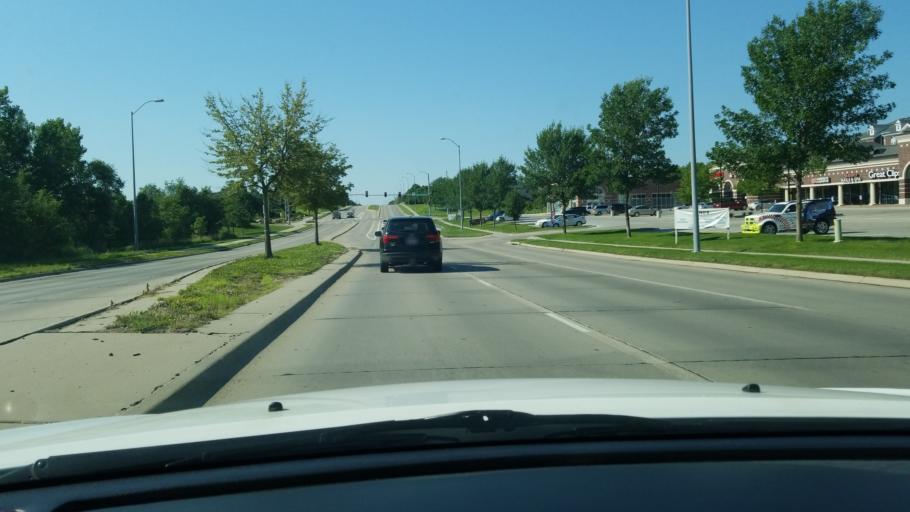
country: US
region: Nebraska
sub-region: Lancaster County
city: Lincoln
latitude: 40.7831
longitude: -96.6061
